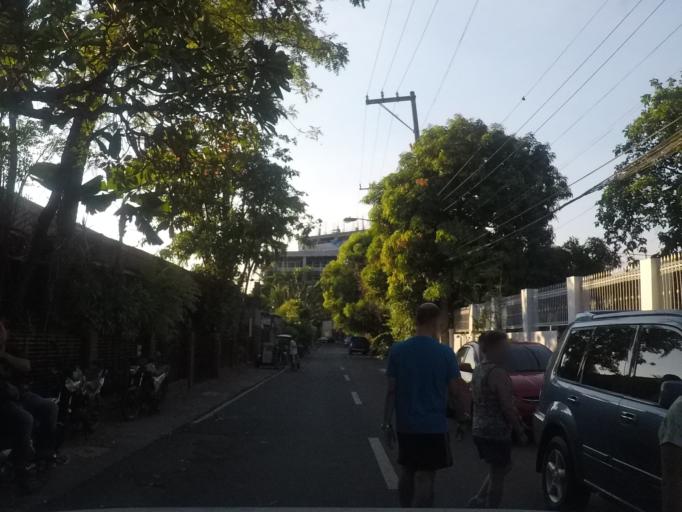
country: PH
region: Metro Manila
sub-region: San Juan
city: San Juan
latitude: 14.6025
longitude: 121.0351
